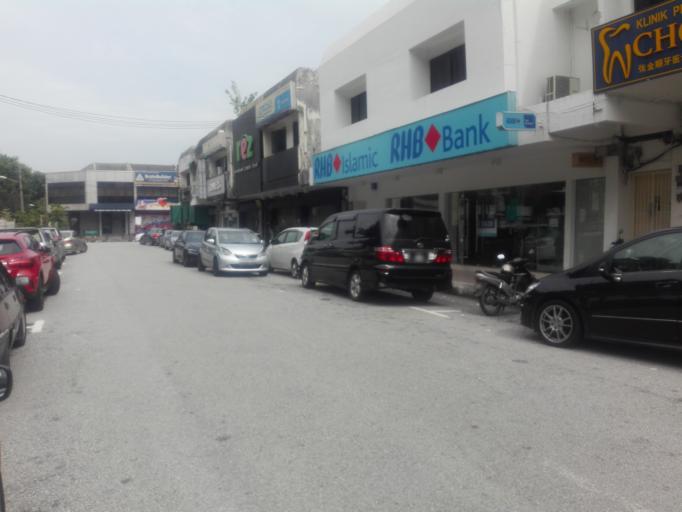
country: MY
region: Perak
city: Ipoh
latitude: 4.6061
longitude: 101.1198
